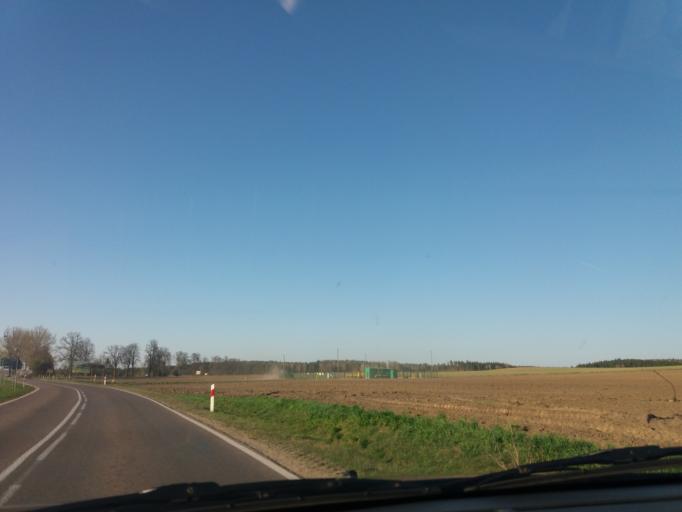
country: PL
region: Warmian-Masurian Voivodeship
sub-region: Powiat nidzicki
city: Nidzica
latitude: 53.3797
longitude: 20.4317
